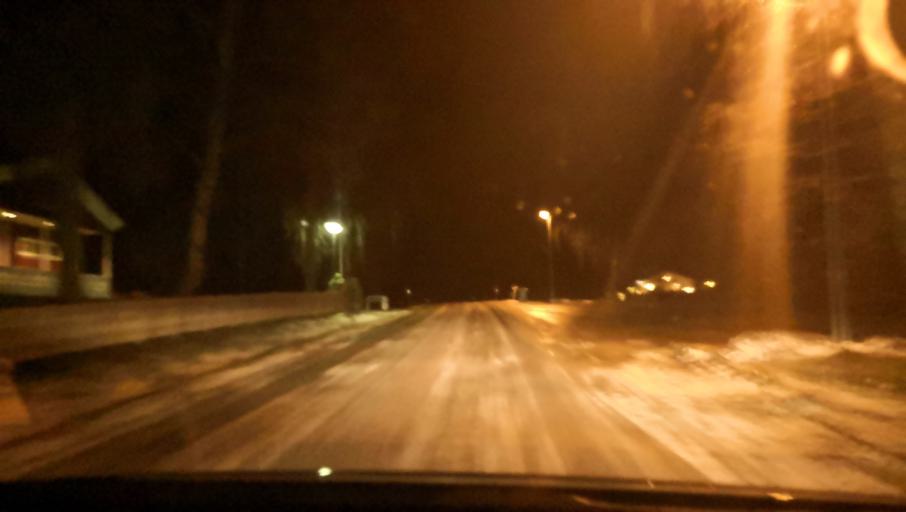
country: SE
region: Vaestmanland
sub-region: Vasteras
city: Tillberga
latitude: 59.6788
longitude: 16.7167
